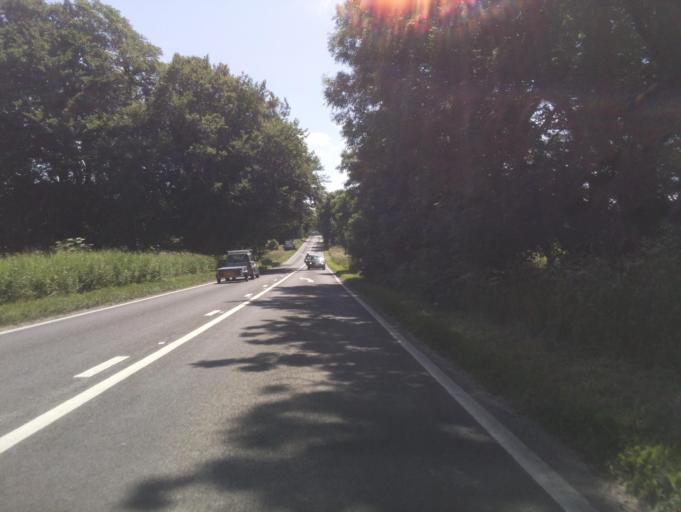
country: GB
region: England
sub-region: Derbyshire
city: Buxton
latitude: 53.2376
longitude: -1.8910
